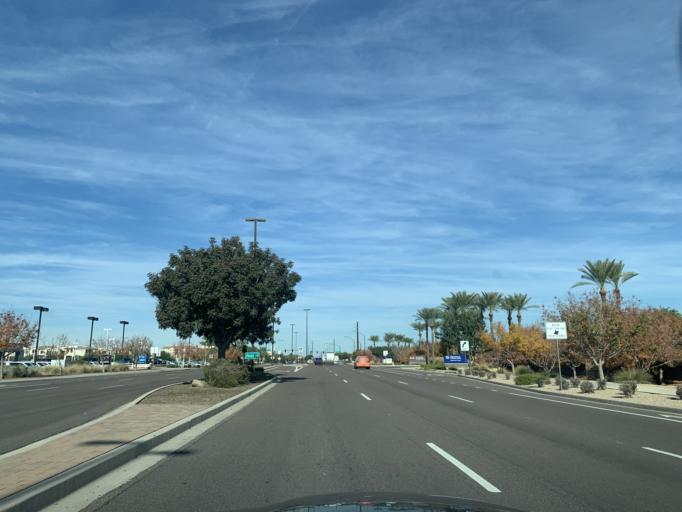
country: US
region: Arizona
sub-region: Maricopa County
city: Gilbert
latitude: 33.2930
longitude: -111.7555
